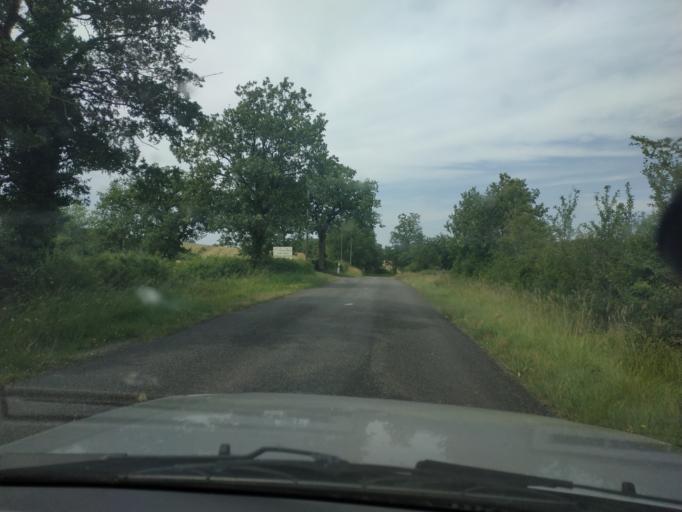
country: FR
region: Midi-Pyrenees
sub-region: Departement du Lot
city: Gramat
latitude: 44.6102
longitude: 1.6229
